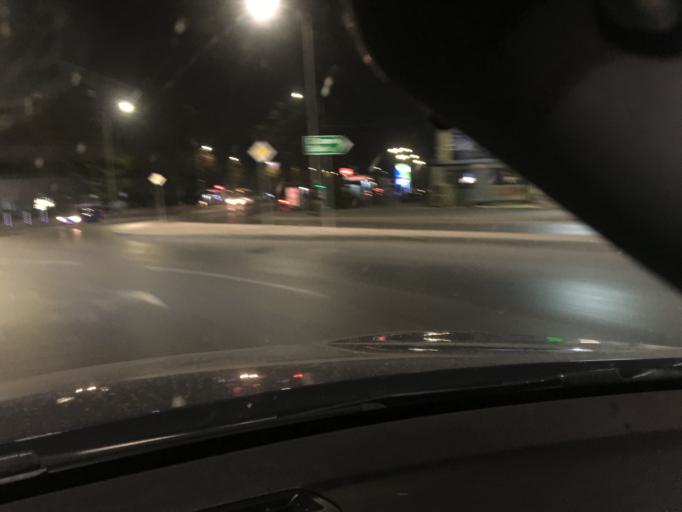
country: BG
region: Varna
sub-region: Obshtina Varna
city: Varna
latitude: 43.2153
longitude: 27.8977
